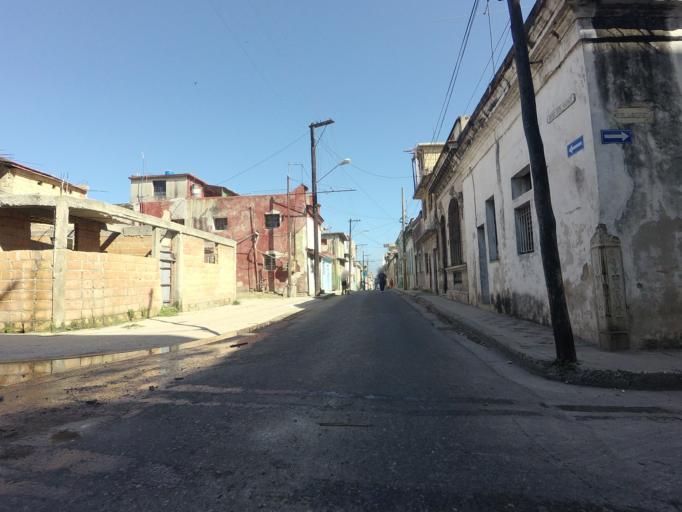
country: CU
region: La Habana
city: Cerro
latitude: 23.1174
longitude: -82.3727
